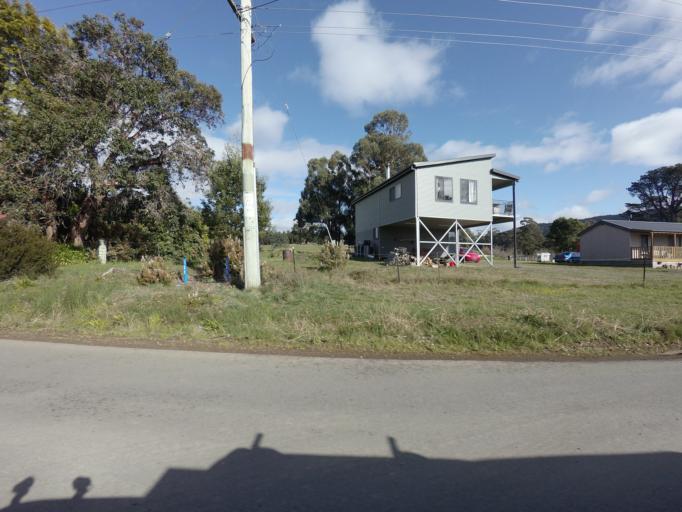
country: AU
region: Tasmania
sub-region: Huon Valley
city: Geeveston
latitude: -43.3357
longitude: 146.9710
